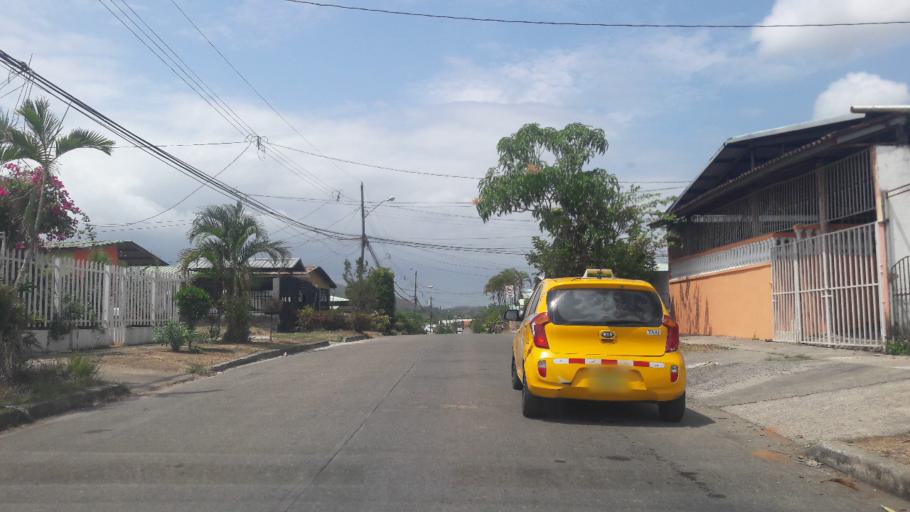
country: PA
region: Panama
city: Alcalde Diaz
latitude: 9.1380
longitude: -79.5505
